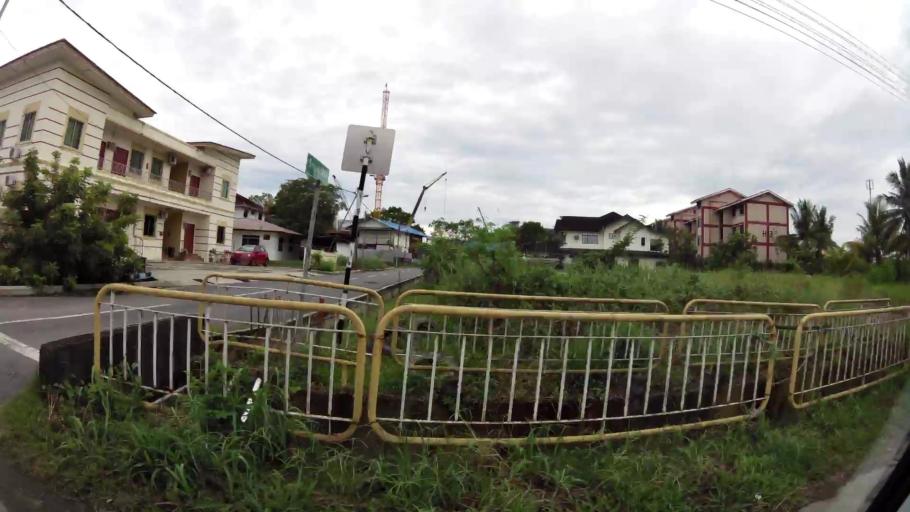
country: BN
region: Brunei and Muara
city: Bandar Seri Begawan
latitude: 4.8973
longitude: 114.9282
